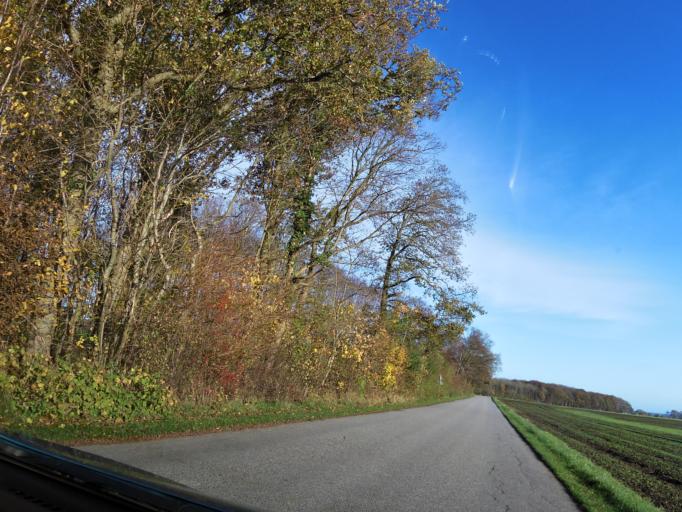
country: DK
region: Central Jutland
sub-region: Odder Kommune
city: Odder
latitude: 55.9144
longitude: 10.2347
